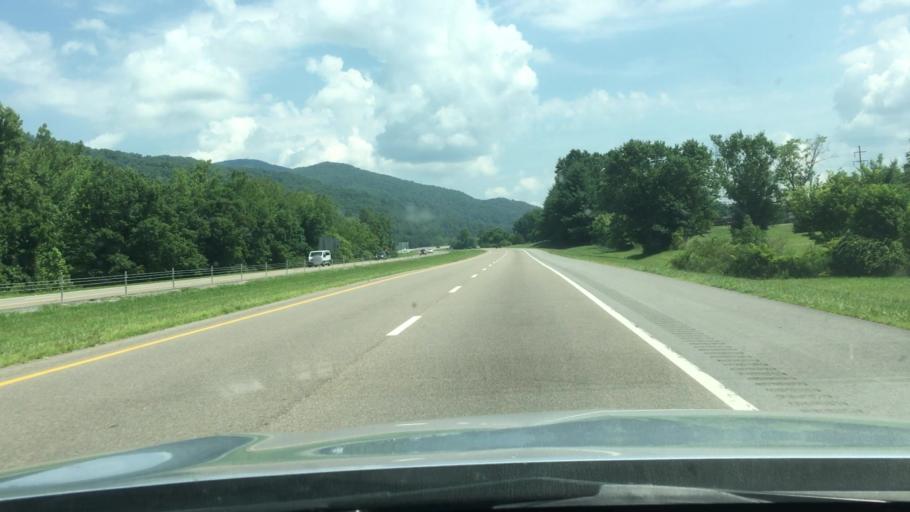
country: US
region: Tennessee
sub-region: Unicoi County
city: Unicoi
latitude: 36.1764
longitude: -82.3842
